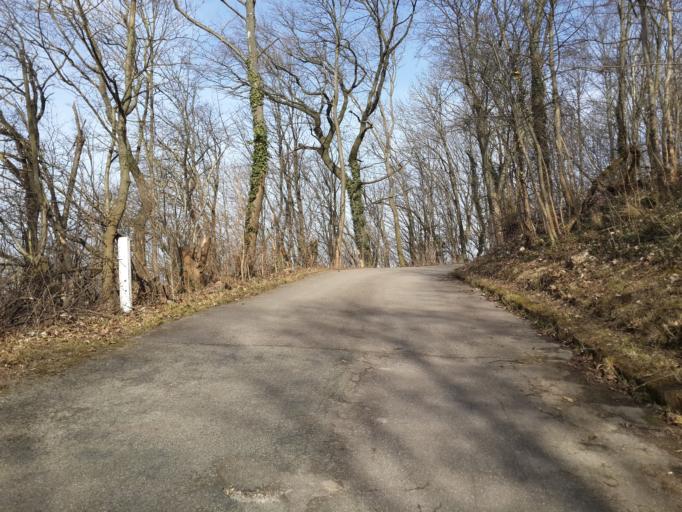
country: DE
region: Baden-Wuerttemberg
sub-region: Regierungsbezirk Stuttgart
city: Heilbronn
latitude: 49.1597
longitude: 9.2337
